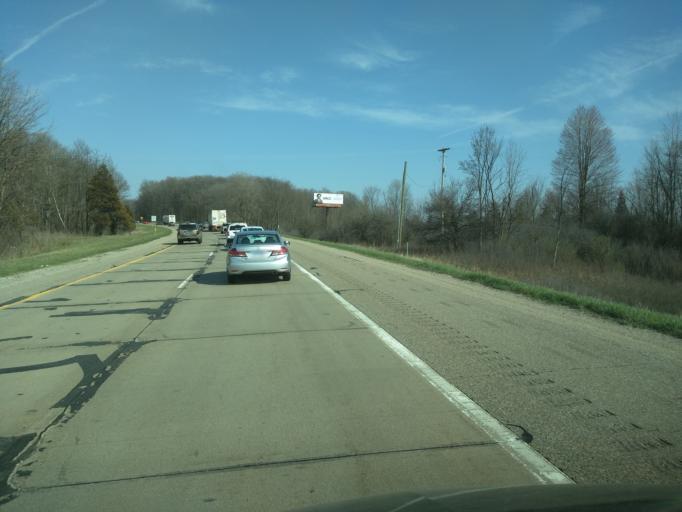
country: US
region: Michigan
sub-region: Kent County
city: Forest Hills
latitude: 42.8901
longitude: -85.5028
